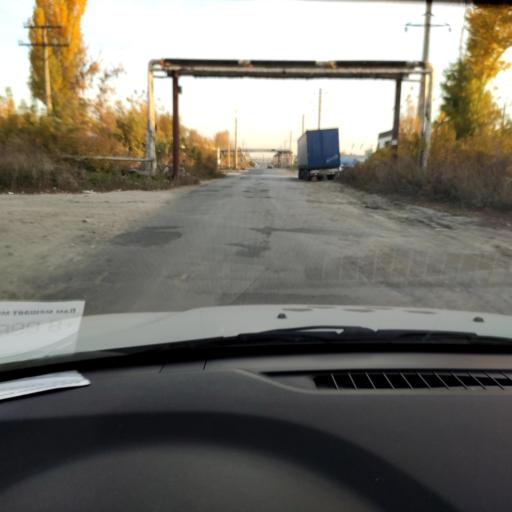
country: RU
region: Samara
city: Tol'yatti
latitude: 53.5296
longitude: 49.4618
